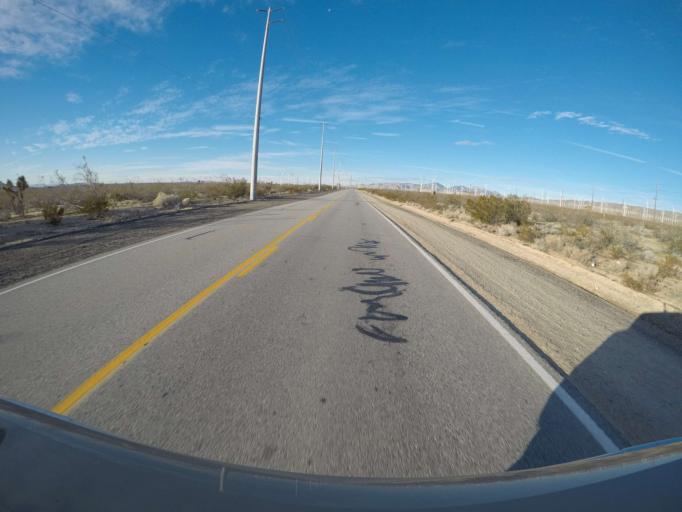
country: US
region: California
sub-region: Kern County
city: Mojave
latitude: 35.0531
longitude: -118.1958
